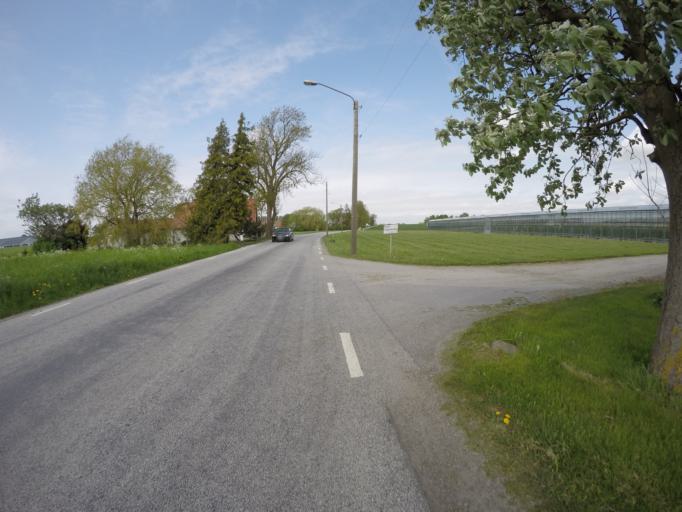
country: SE
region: Skane
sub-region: Malmo
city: Tygelsjo
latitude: 55.5305
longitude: 13.0259
